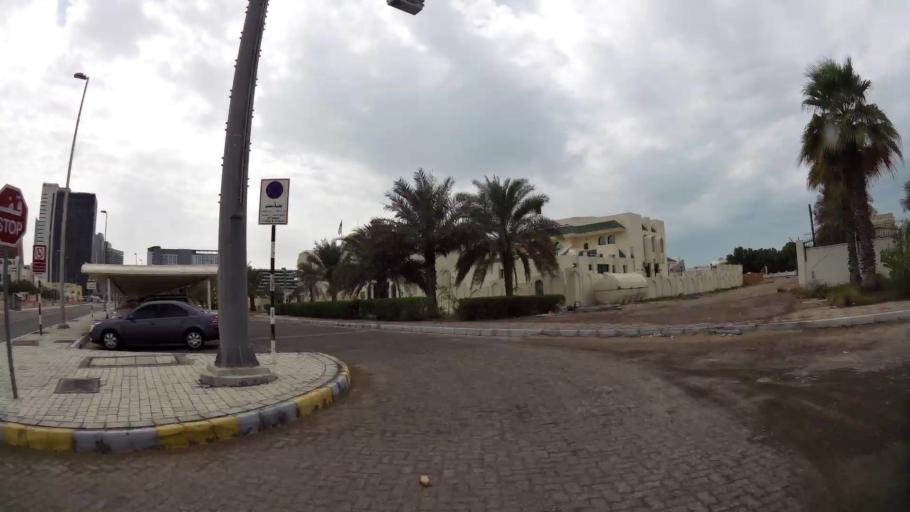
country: AE
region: Abu Dhabi
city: Abu Dhabi
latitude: 24.4253
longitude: 54.4409
